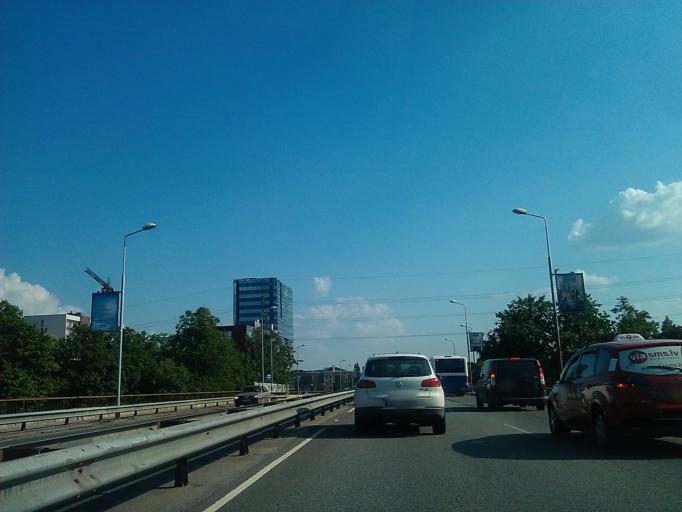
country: LV
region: Riga
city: Jaunciems
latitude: 56.9795
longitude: 24.1629
